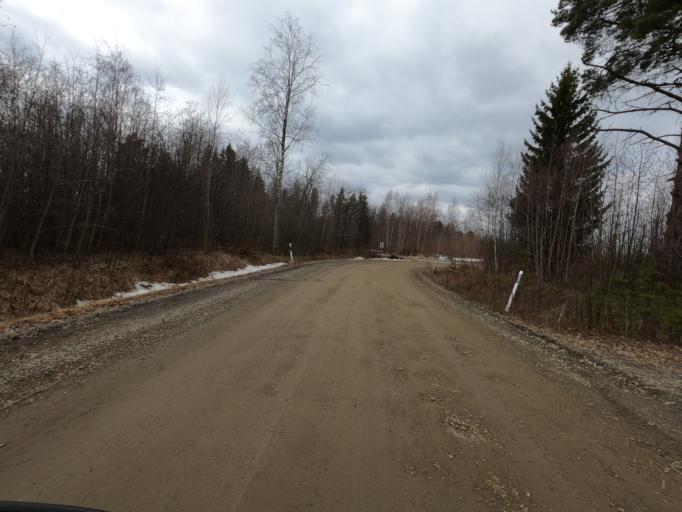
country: FI
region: North Karelia
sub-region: Joensuu
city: Joensuu
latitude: 62.5659
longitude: 29.8005
